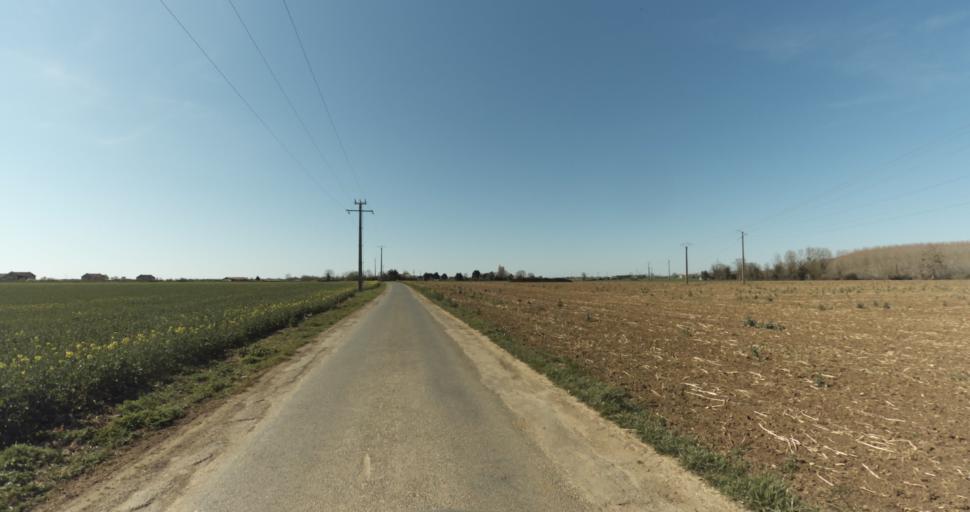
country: FR
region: Lower Normandy
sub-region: Departement du Calvados
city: Saint-Pierre-sur-Dives
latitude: 49.0510
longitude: -0.0415
